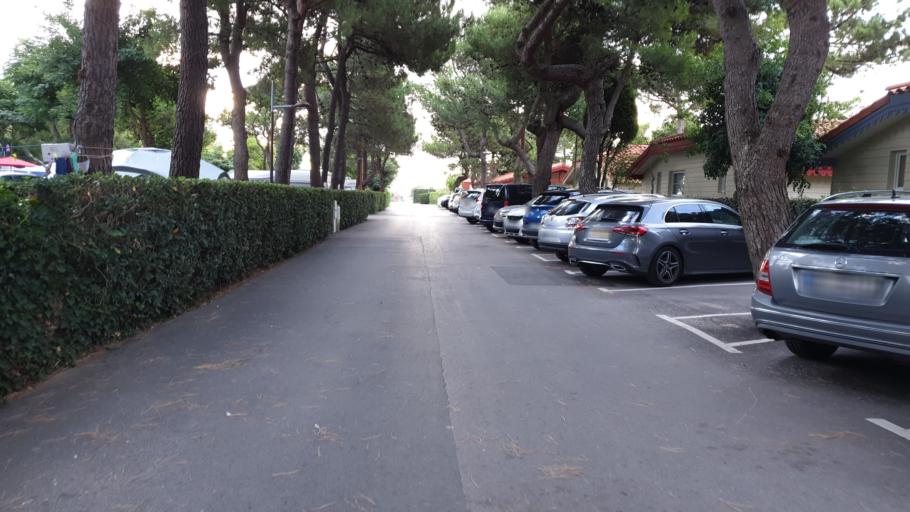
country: FR
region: Languedoc-Roussillon
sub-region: Departement des Pyrenees-Orientales
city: Sainte-Marie-Plage
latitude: 42.7098
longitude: 3.0361
